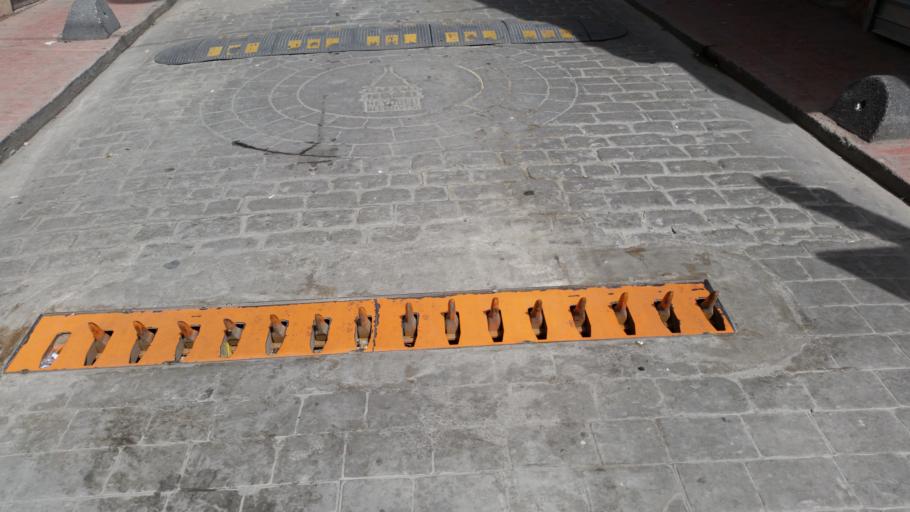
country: TR
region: Istanbul
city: Eminoenue
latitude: 41.0334
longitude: 28.9709
